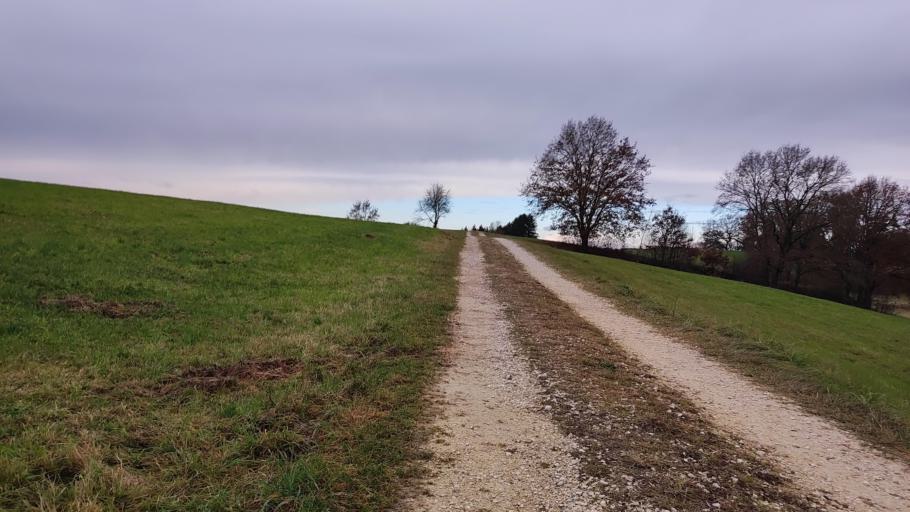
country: DE
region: Bavaria
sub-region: Swabia
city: Altenmunster
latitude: 48.4578
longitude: 10.6026
